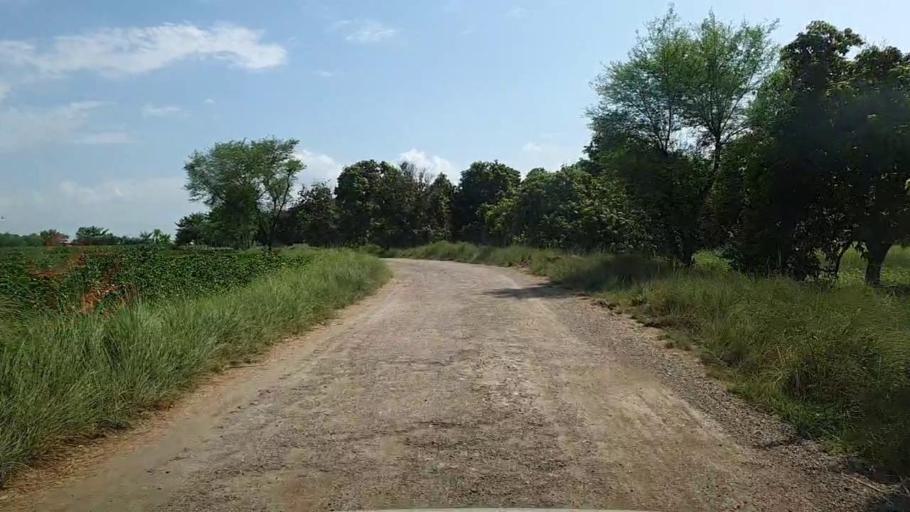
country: PK
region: Sindh
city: Bhiria
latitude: 26.9079
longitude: 68.2255
